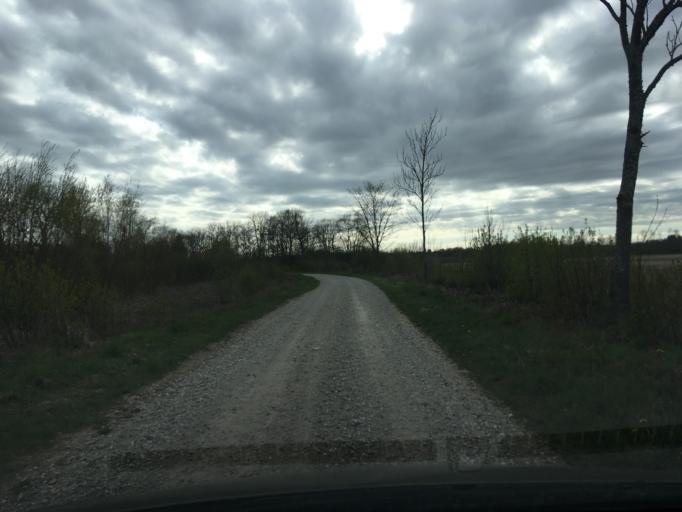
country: EE
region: Laeaene
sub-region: Lihula vald
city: Lihula
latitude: 58.5780
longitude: 23.7256
